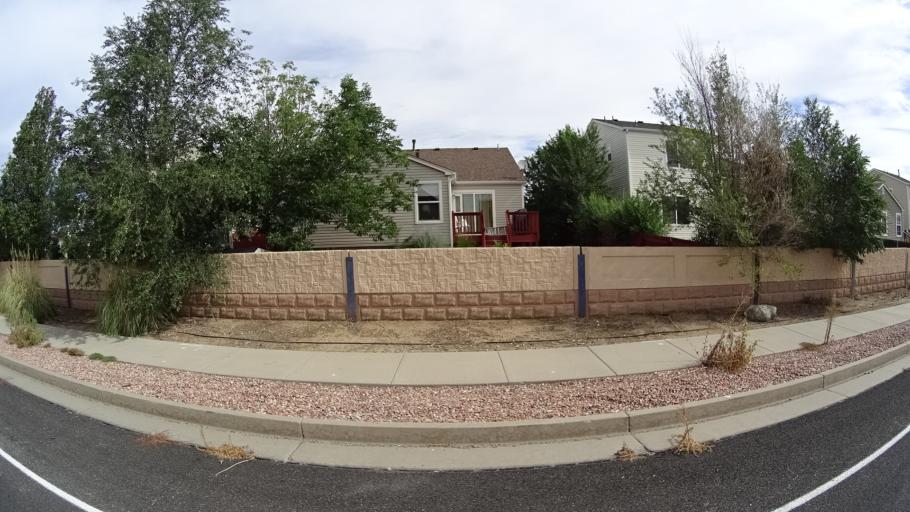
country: US
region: Colorado
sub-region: El Paso County
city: Fountain
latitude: 38.7084
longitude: -104.6941
